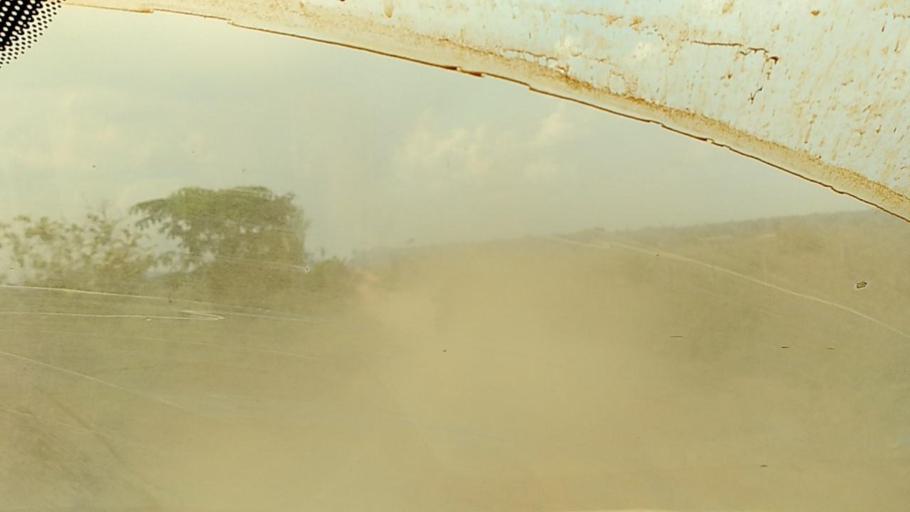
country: BR
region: Rondonia
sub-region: Porto Velho
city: Porto Velho
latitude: -8.6924
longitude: -63.2392
